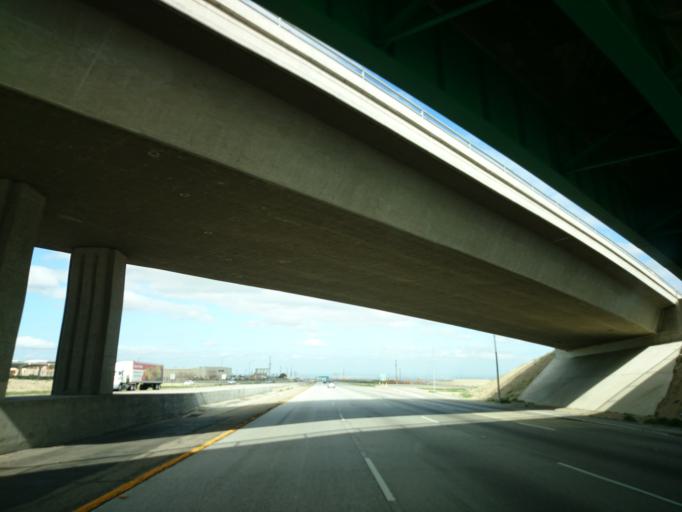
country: US
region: California
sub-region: Kern County
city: Frazier Park
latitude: 34.9864
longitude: -118.9452
